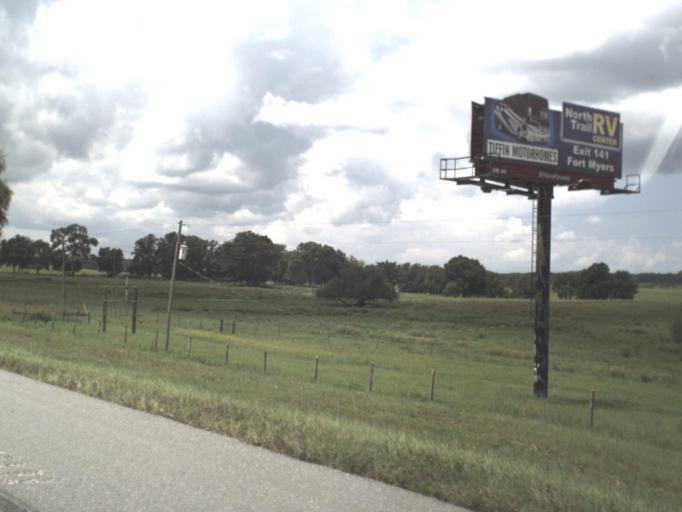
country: US
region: Florida
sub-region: Hernando County
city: Hill 'n Dale
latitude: 28.4957
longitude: -82.2487
